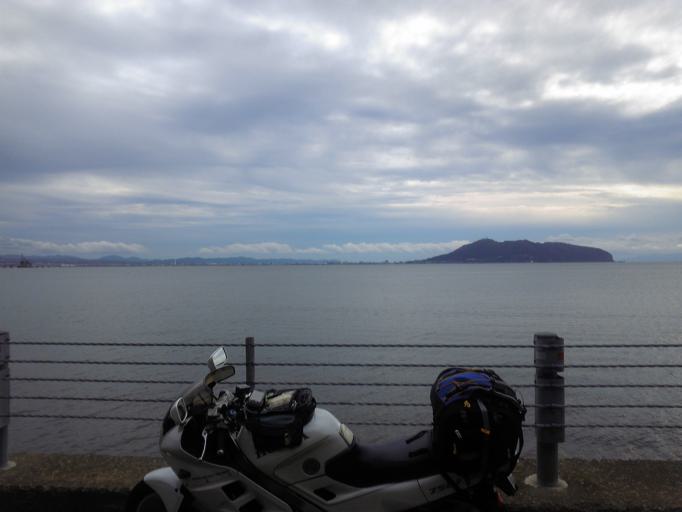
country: JP
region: Hokkaido
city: Kamiiso
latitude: 41.7991
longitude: 140.6191
